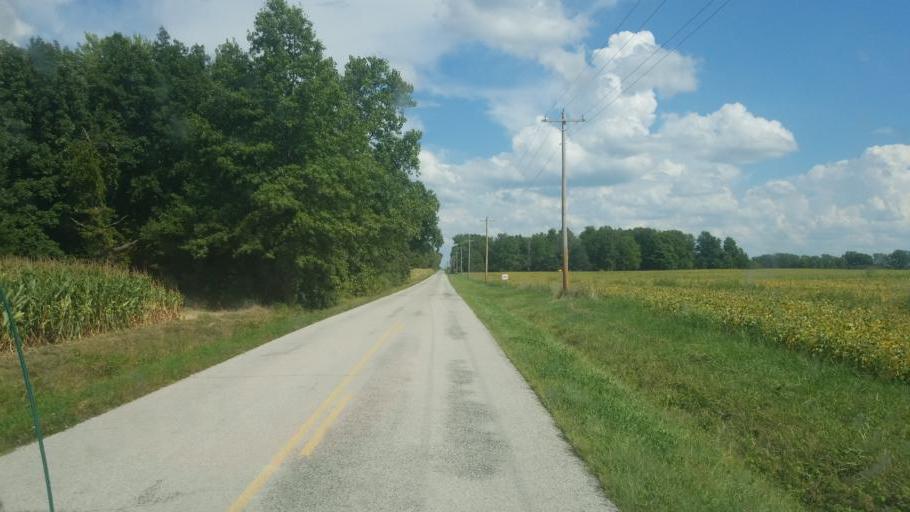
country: US
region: Ohio
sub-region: Seneca County
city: Tiffin
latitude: 40.9935
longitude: -83.1098
